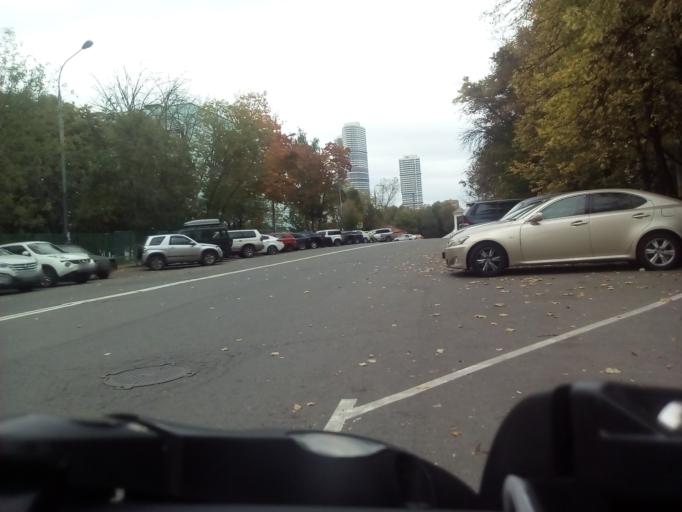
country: RU
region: Moscow
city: Rostokino
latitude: 55.8263
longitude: 37.6531
